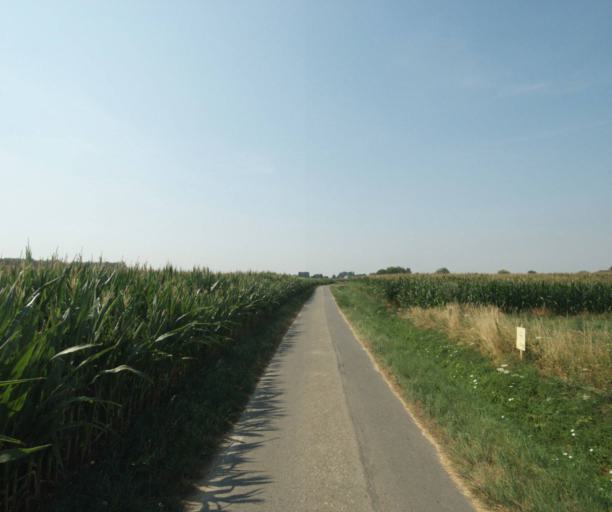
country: FR
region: Nord-Pas-de-Calais
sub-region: Departement du Nord
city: Quesnoy-sur-Deule
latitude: 50.7101
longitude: 2.9856
